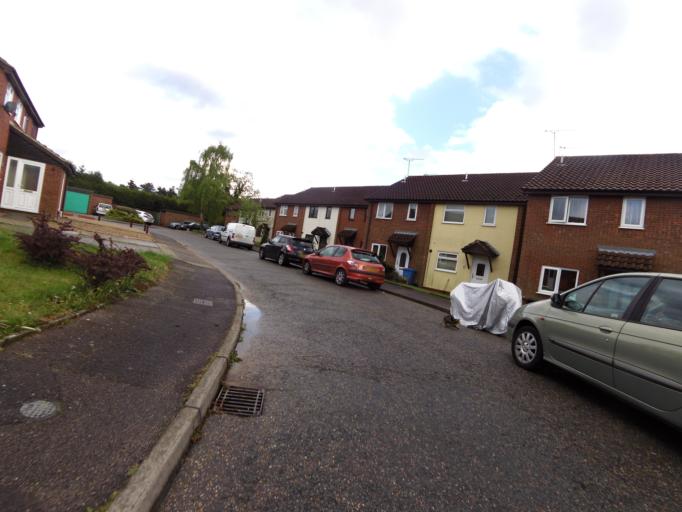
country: GB
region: England
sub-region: Suffolk
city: Ipswich
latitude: 52.0478
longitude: 1.1891
